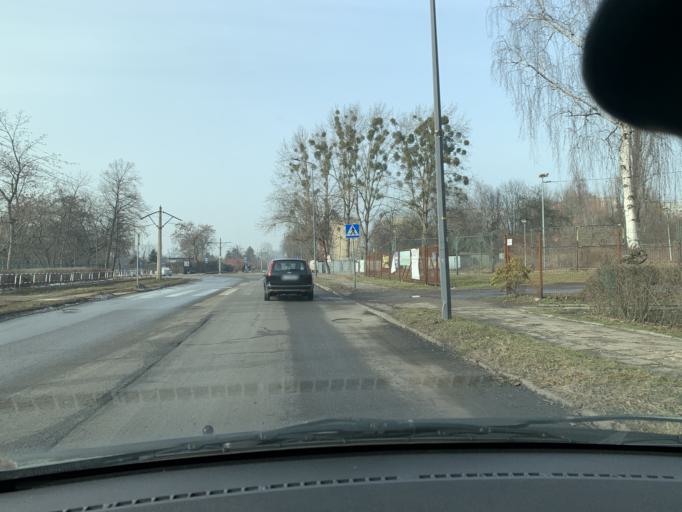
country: PL
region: Silesian Voivodeship
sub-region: Bytom
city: Bytom
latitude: 50.3546
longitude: 18.9073
